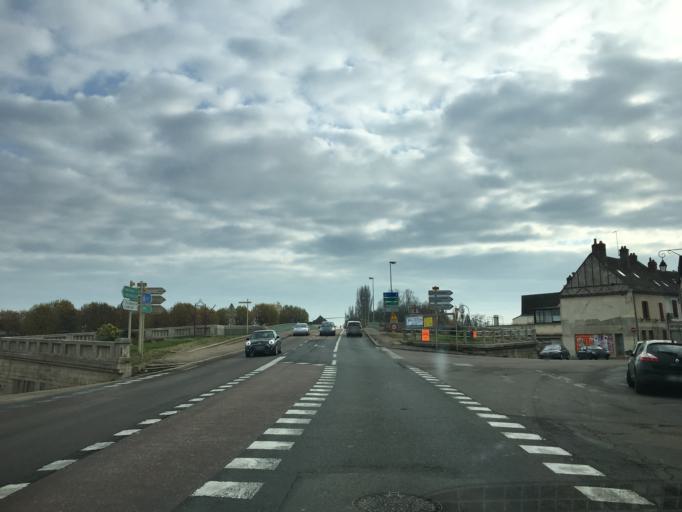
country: FR
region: Bourgogne
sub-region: Departement de l'Yonne
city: Pont-sur-Yonne
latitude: 48.2885
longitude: 3.2046
